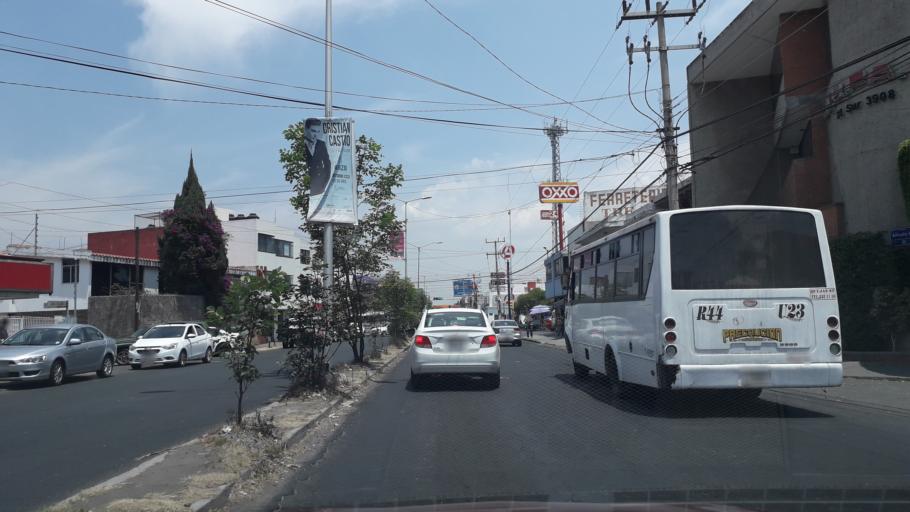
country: MX
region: Puebla
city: Puebla
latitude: 19.0202
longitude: -98.1921
